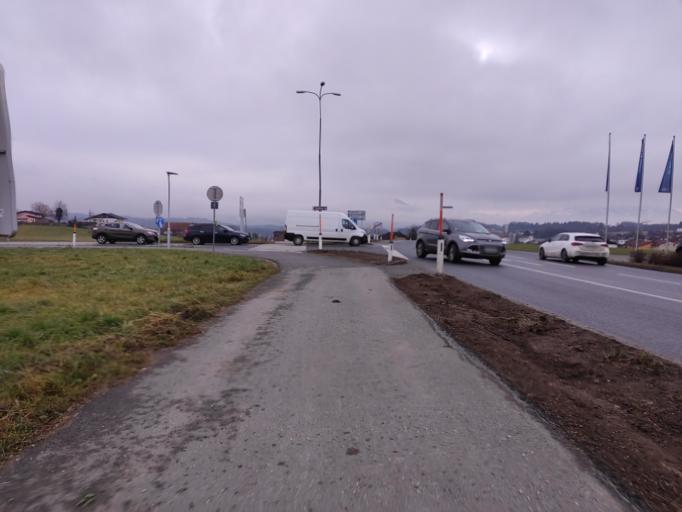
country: AT
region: Salzburg
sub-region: Politischer Bezirk Salzburg-Umgebung
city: Seekirchen am Wallersee
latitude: 47.9032
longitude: 13.1209
